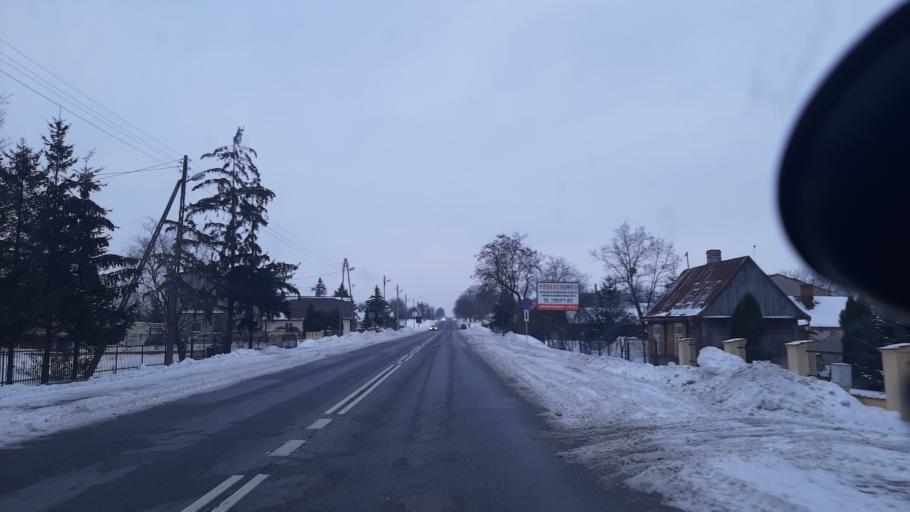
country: PL
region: Lublin Voivodeship
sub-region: Powiat pulawski
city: Markuszow
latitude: 51.3736
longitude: 22.2664
